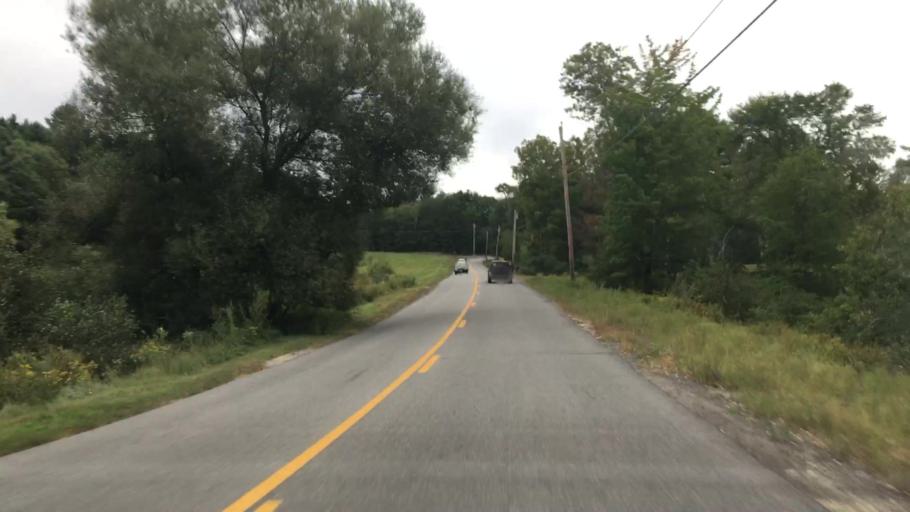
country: US
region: Maine
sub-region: Cumberland County
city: Freeport
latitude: 43.8897
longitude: -70.1780
